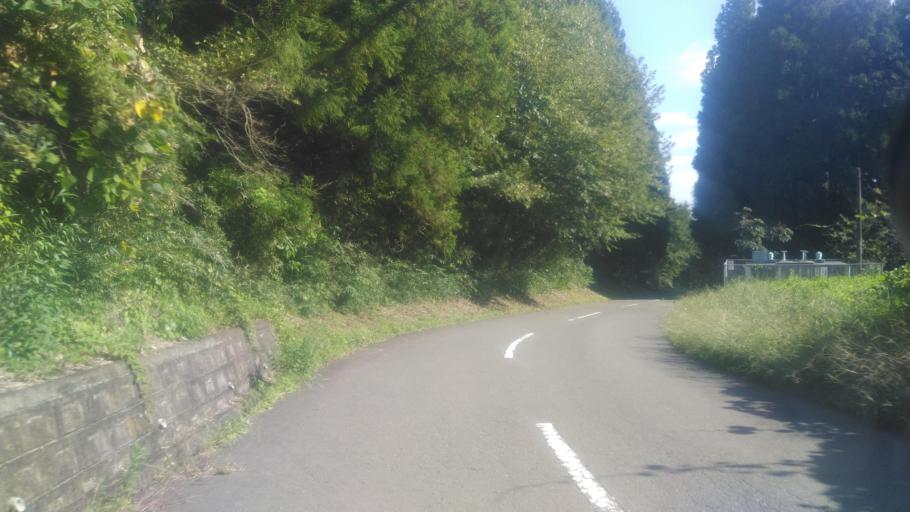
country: JP
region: Miyagi
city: Okawara
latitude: 38.0711
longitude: 140.6881
